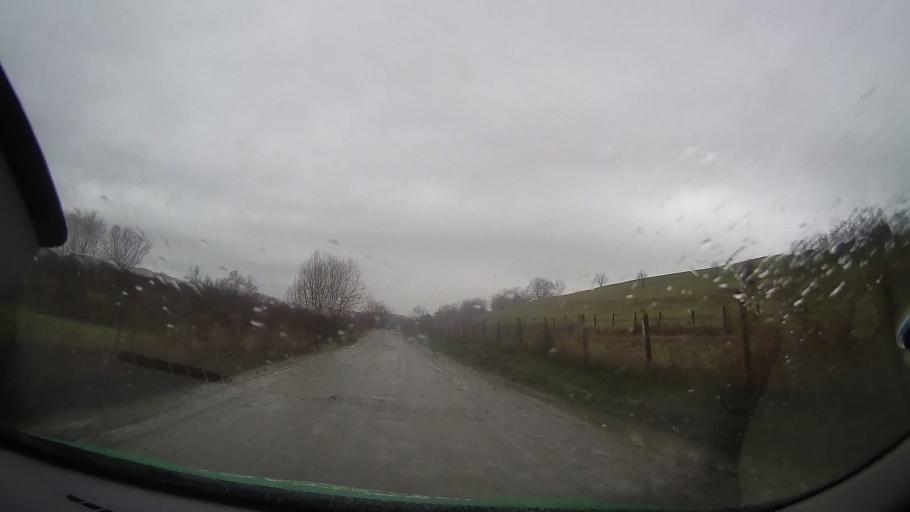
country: RO
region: Bistrita-Nasaud
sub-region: Comuna Monor
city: Monor
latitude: 46.9492
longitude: 24.7076
